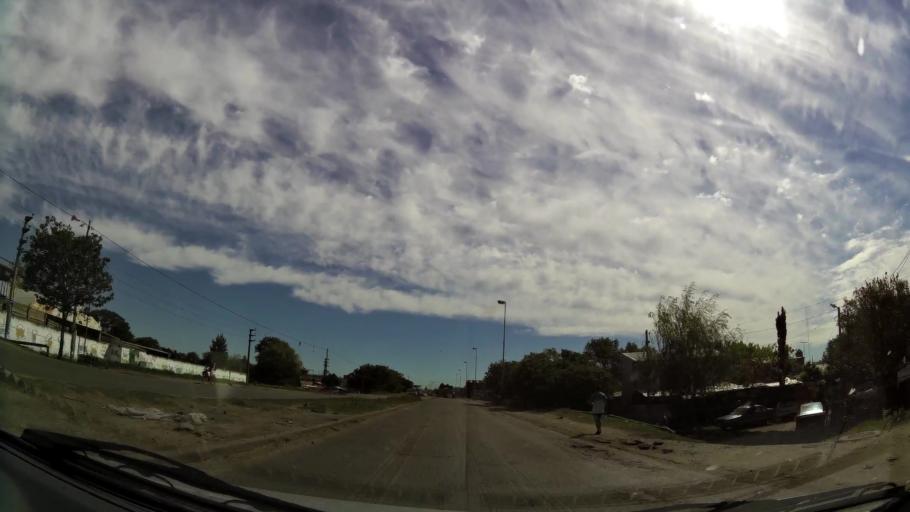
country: AR
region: Buenos Aires
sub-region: Partido de Quilmes
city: Quilmes
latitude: -34.7832
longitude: -58.2980
